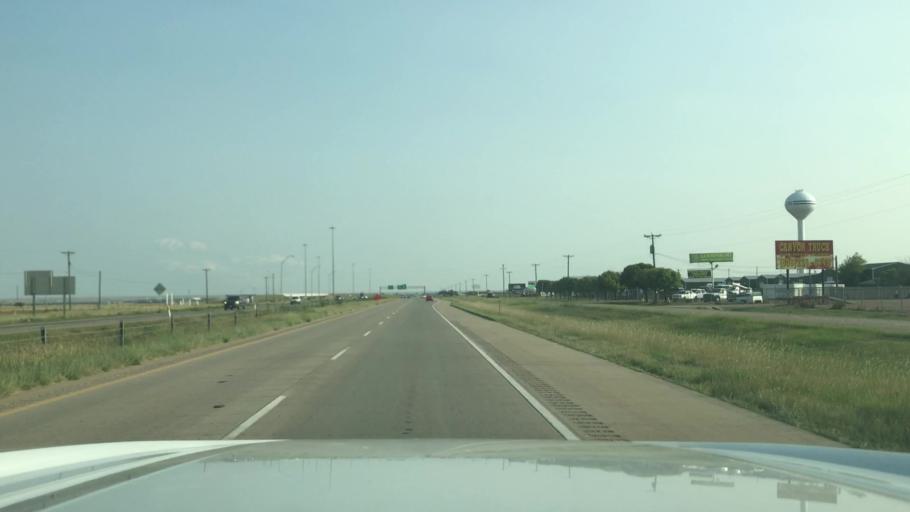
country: US
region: Texas
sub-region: Randall County
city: Canyon
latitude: 35.0318
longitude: -101.9194
